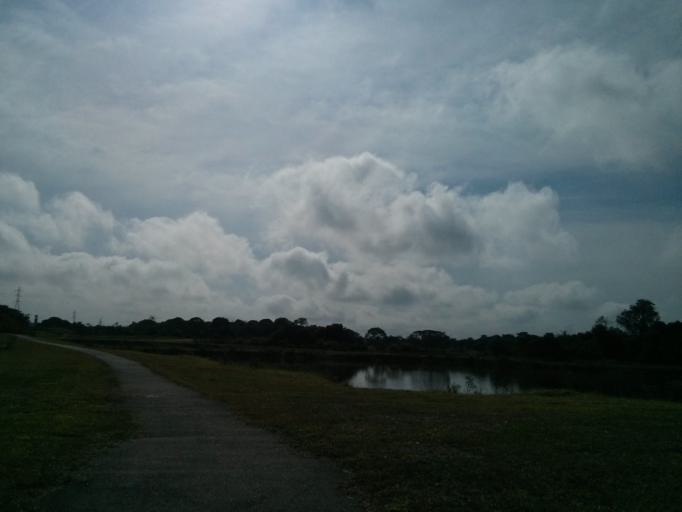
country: BR
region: Parana
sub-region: Sao Jose Dos Pinhais
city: Sao Jose dos Pinhais
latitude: -25.5104
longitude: -49.2156
